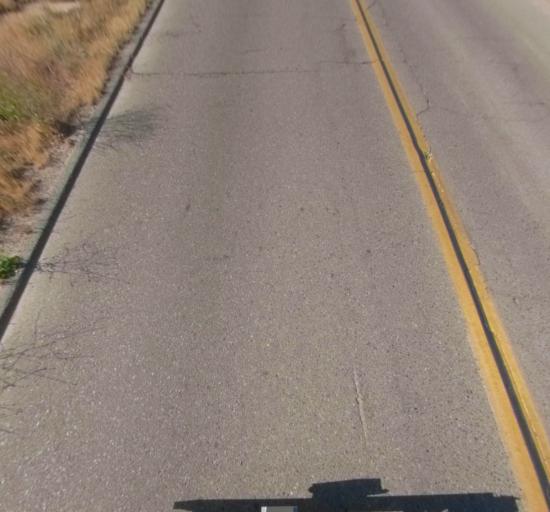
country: US
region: California
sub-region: Madera County
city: Parkwood
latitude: 36.8945
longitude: -120.1286
